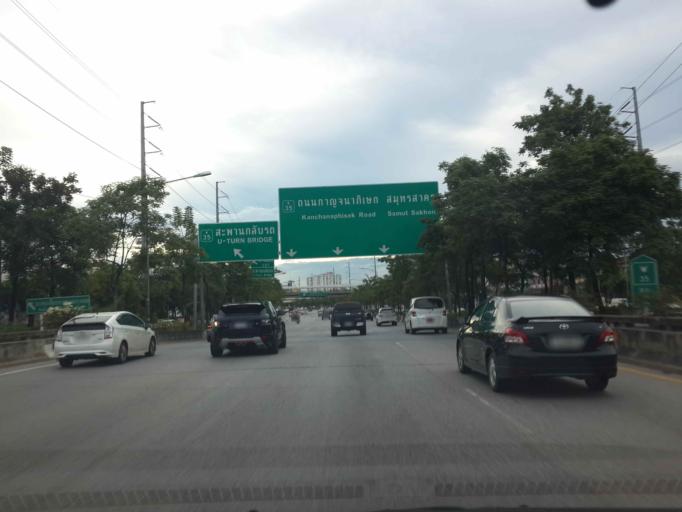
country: TH
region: Bangkok
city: Chom Thong
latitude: 13.6799
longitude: 100.4705
